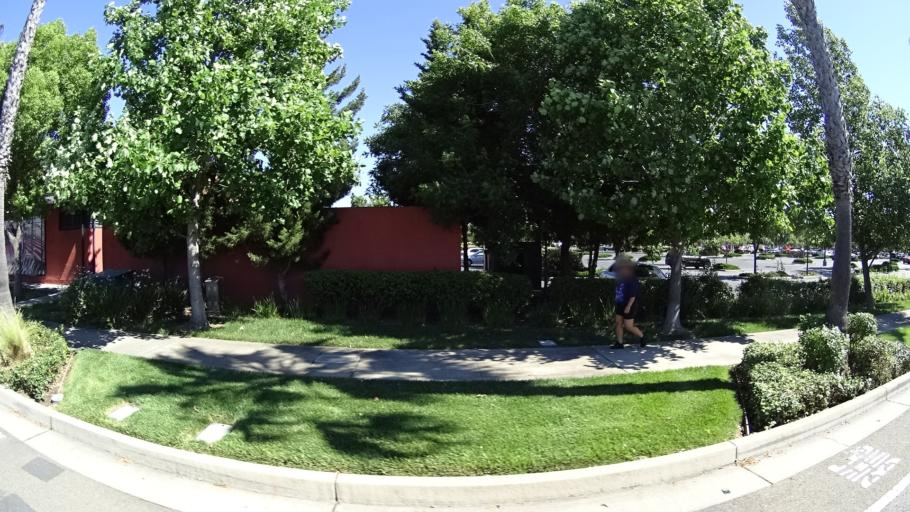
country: US
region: California
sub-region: Sacramento County
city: Sacramento
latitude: 38.6398
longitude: -121.5014
